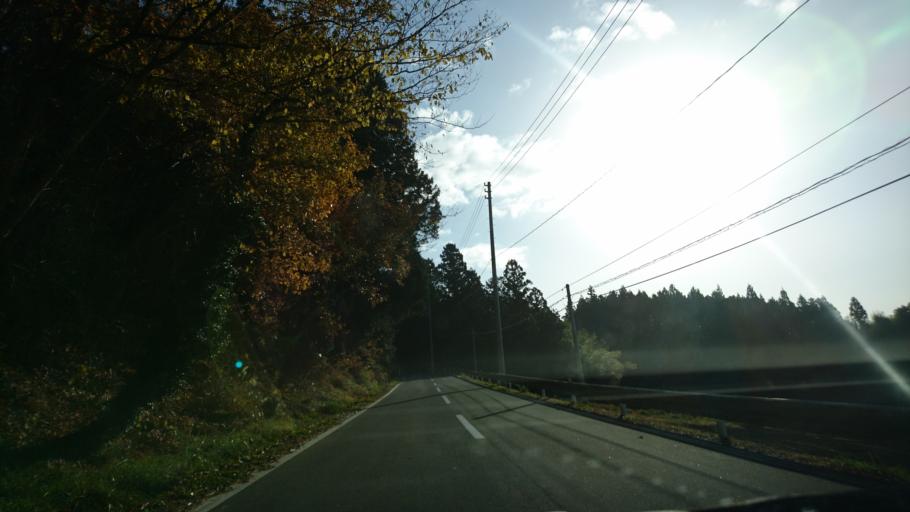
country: JP
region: Iwate
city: Ichinoseki
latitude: 38.8716
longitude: 141.3131
